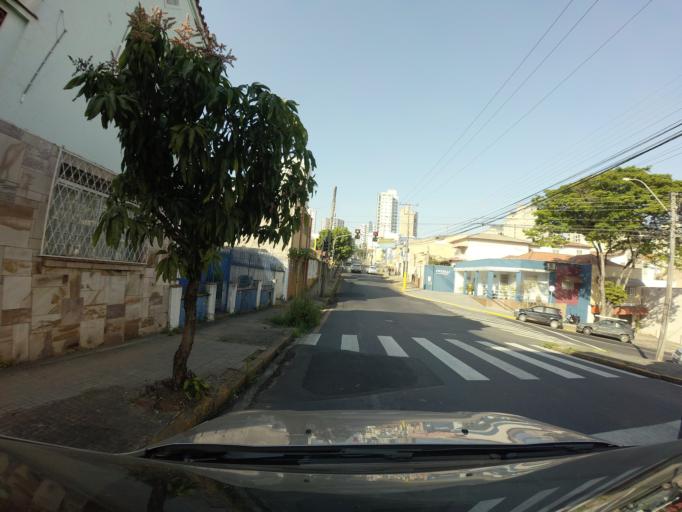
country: BR
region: Sao Paulo
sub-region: Piracicaba
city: Piracicaba
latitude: -22.7280
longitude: -47.6534
